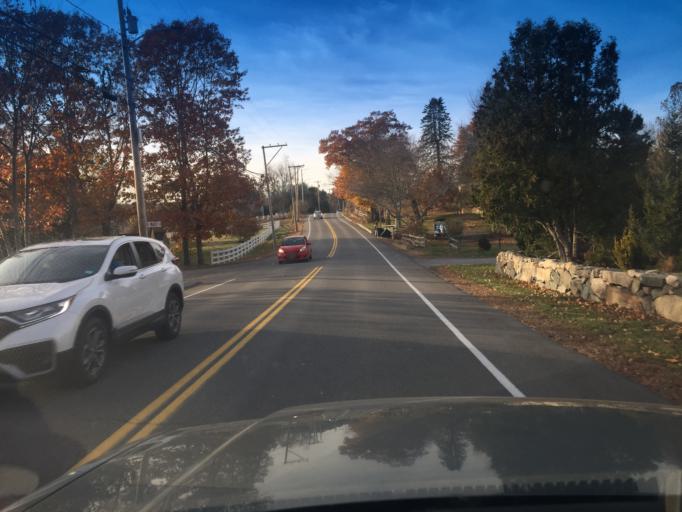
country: US
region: Maine
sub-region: York County
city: York Harbor
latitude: 43.1596
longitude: -70.7013
